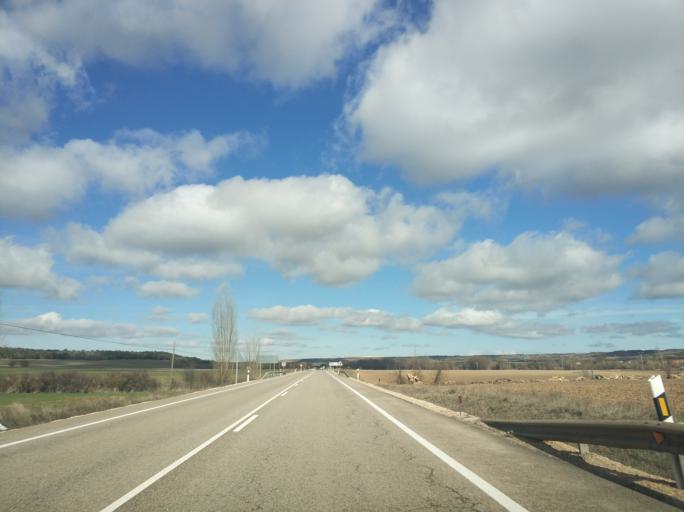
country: ES
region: Castille and Leon
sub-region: Provincia de Burgos
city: Revillarruz
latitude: 42.2388
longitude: -3.6710
